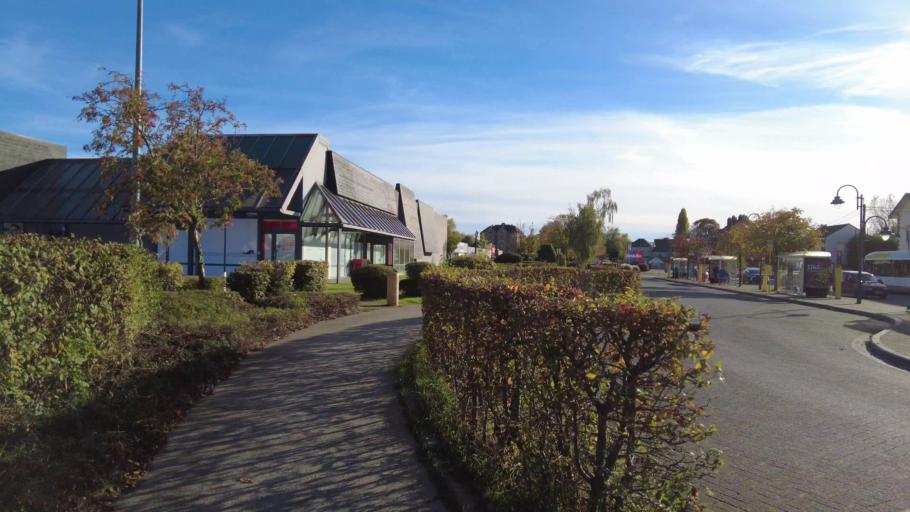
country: BE
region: Wallonia
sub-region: Province du Brabant Wallon
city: Jodoigne
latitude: 50.7235
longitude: 4.8776
